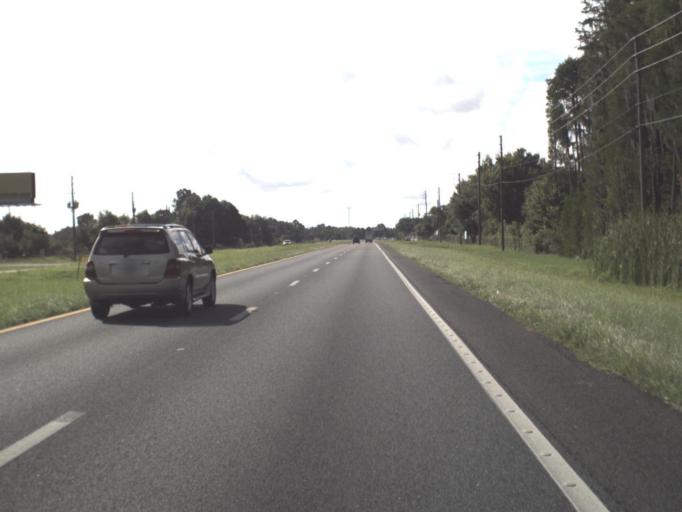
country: US
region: Florida
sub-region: Pasco County
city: Land O' Lakes
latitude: 28.2528
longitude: -82.4688
